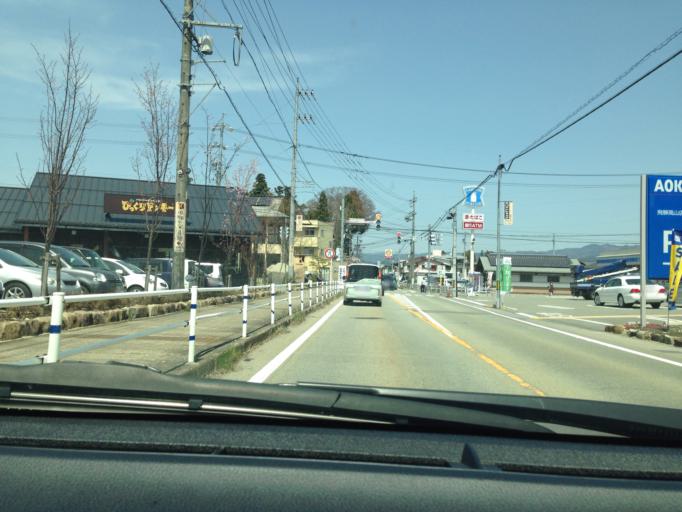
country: JP
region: Gifu
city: Takayama
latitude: 36.1334
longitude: 137.2556
